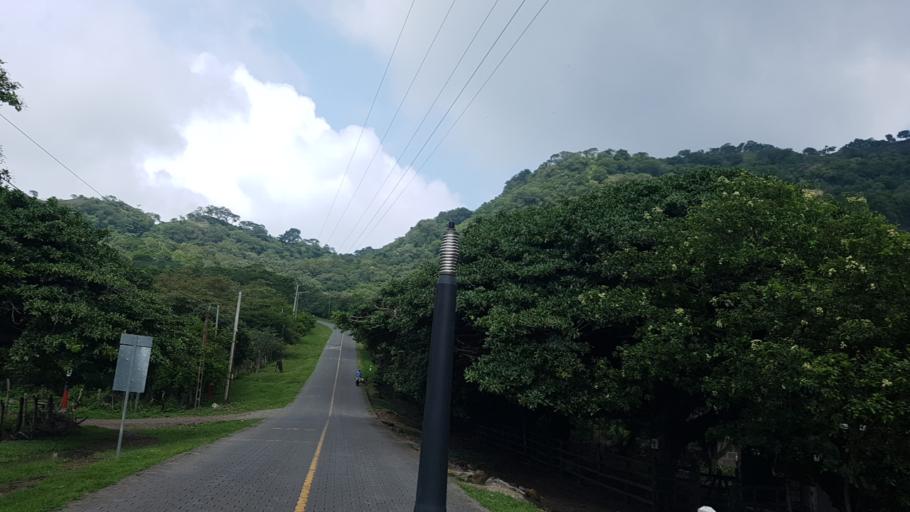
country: NI
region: Leon
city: Santa Rosa del Penon
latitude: 12.9339
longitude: -86.3415
